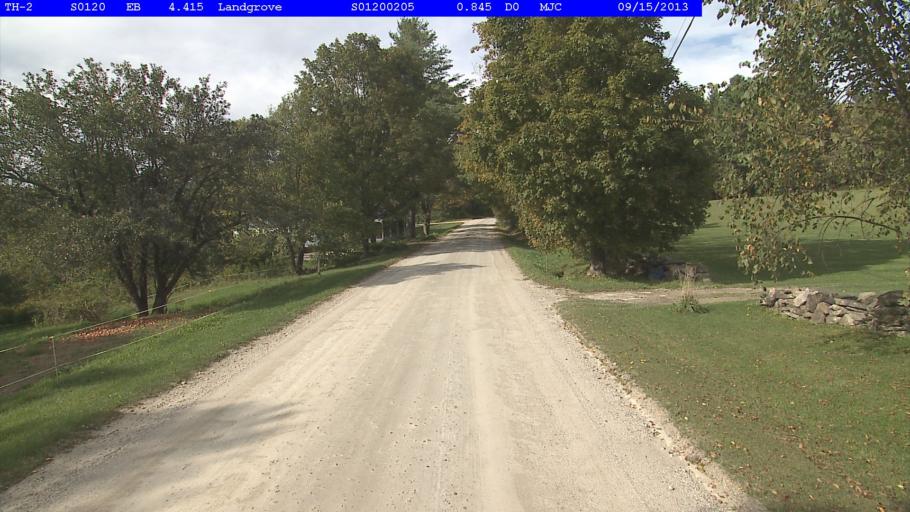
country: US
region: Vermont
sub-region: Bennington County
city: Manchester Center
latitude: 43.2719
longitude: -72.8616
